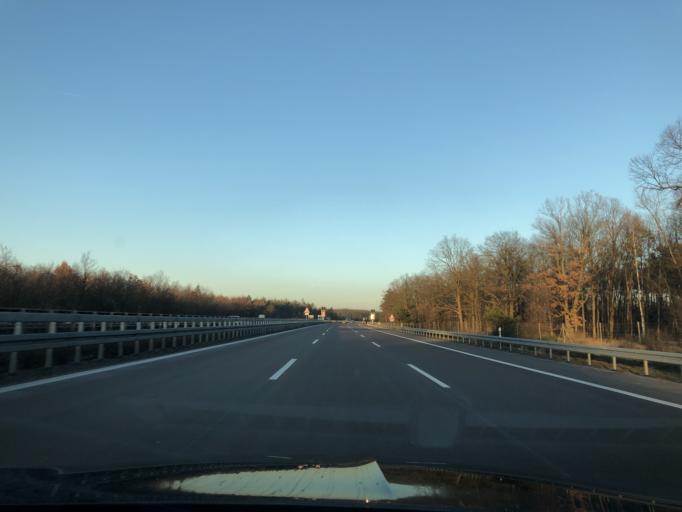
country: DE
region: Saxony-Anhalt
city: Raguhn
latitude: 51.7609
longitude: 12.2349
